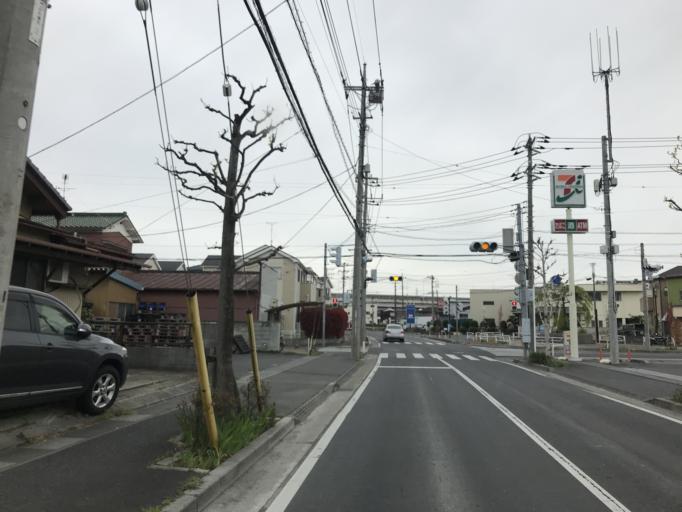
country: JP
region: Saitama
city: Yashio-shi
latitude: 35.8233
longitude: 139.8479
